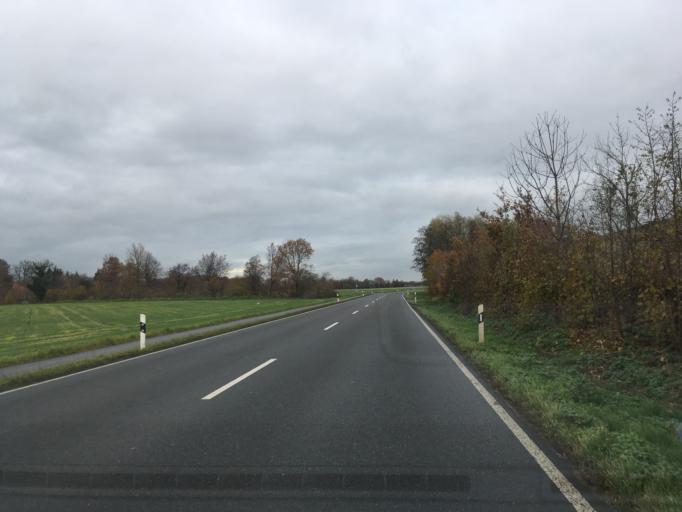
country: DE
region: North Rhine-Westphalia
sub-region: Regierungsbezirk Munster
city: Gescher
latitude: 51.9826
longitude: 7.0267
